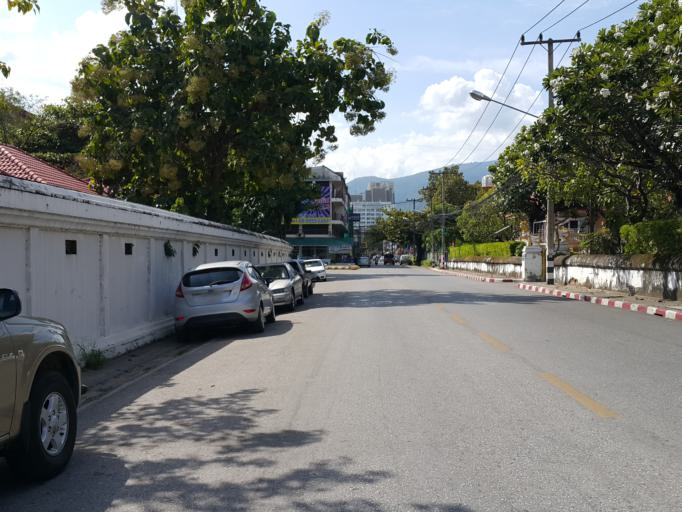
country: TH
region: Chiang Mai
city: Chiang Mai
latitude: 18.7895
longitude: 98.9812
